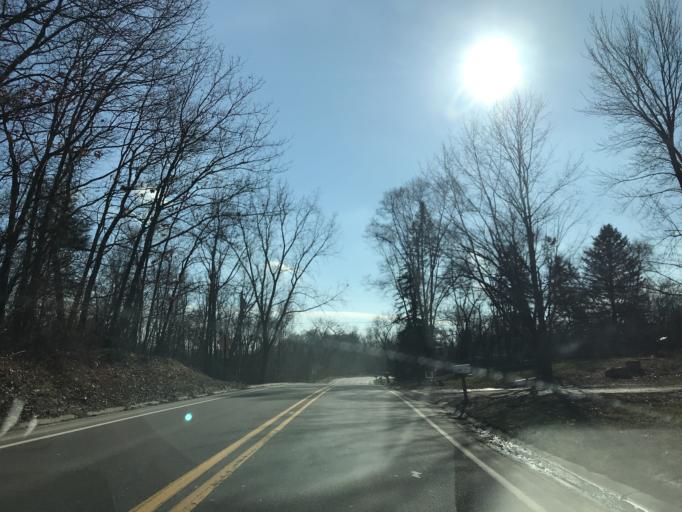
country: US
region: Michigan
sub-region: Livingston County
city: Whitmore Lake
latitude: 42.4416
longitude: -83.7404
